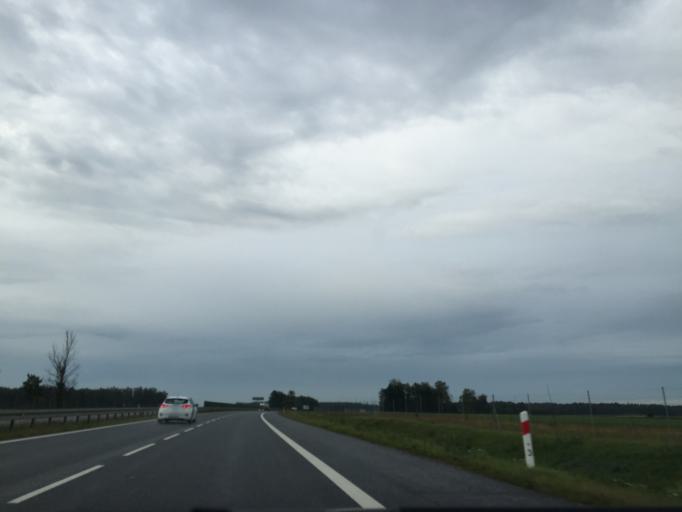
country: PL
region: Podlasie
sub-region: Powiat zambrowski
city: Zambrow
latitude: 53.0160
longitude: 22.3096
